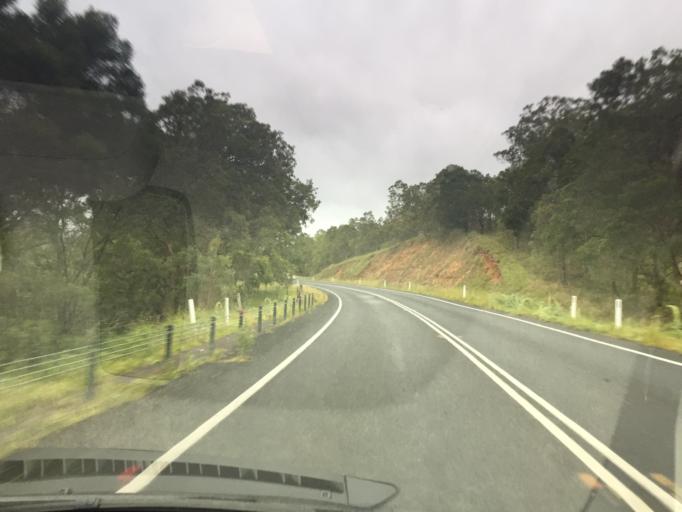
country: AU
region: New South Wales
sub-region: Bega Valley
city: Bega
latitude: -36.6179
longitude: 149.5184
